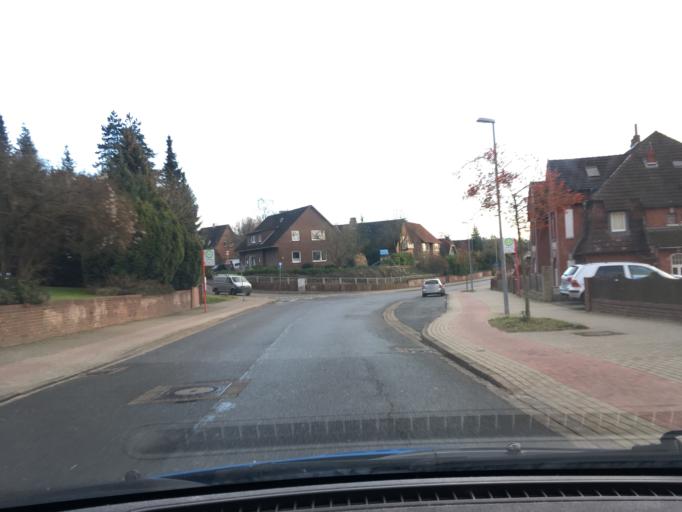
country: DE
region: Lower Saxony
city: Lueneburg
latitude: 53.2436
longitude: 10.4226
